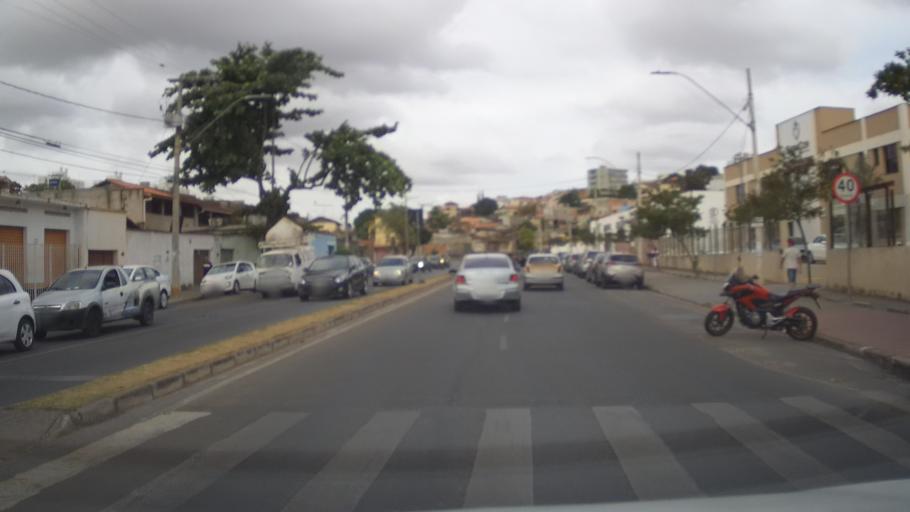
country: BR
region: Minas Gerais
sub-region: Belo Horizonte
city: Belo Horizonte
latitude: -19.8298
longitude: -43.9719
